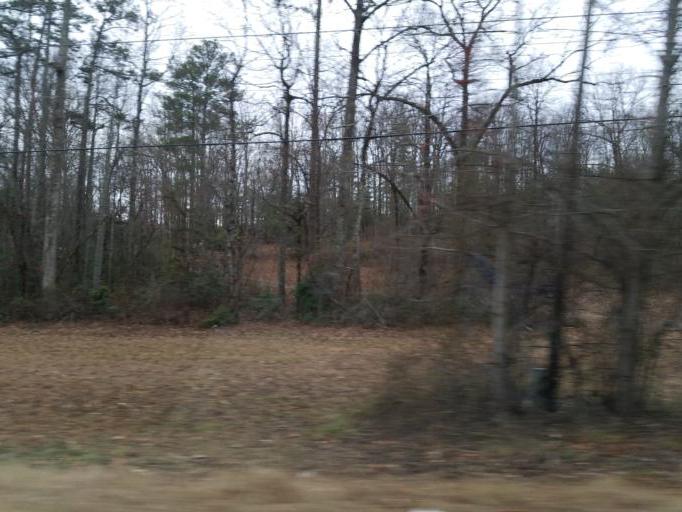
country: US
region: Georgia
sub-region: Dawson County
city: Dawsonville
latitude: 34.5169
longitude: -84.2415
